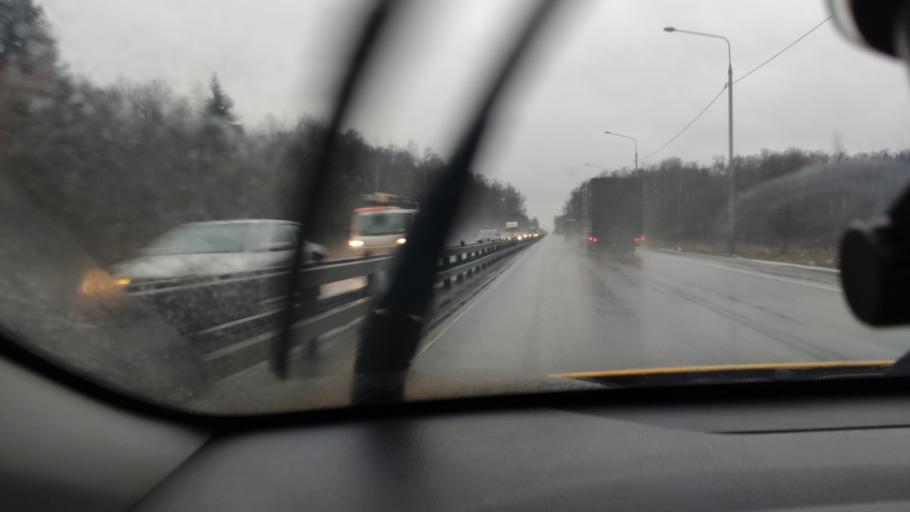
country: RU
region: Moskovskaya
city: Troitsk
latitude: 55.3631
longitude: 37.3676
